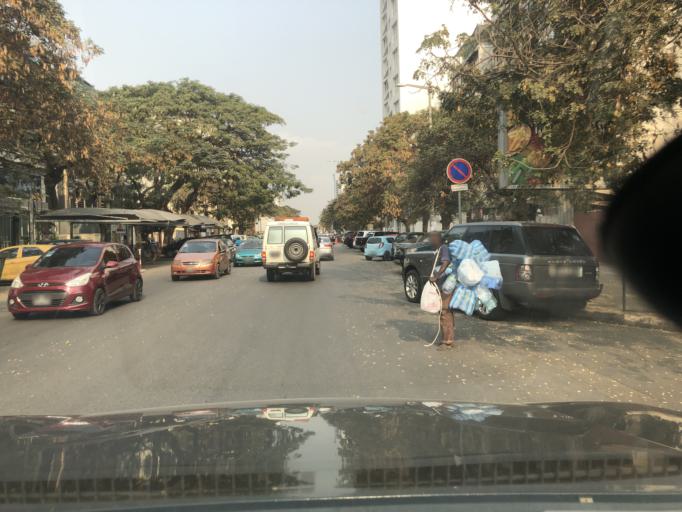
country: AO
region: Luanda
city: Luanda
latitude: -8.8210
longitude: 13.2484
